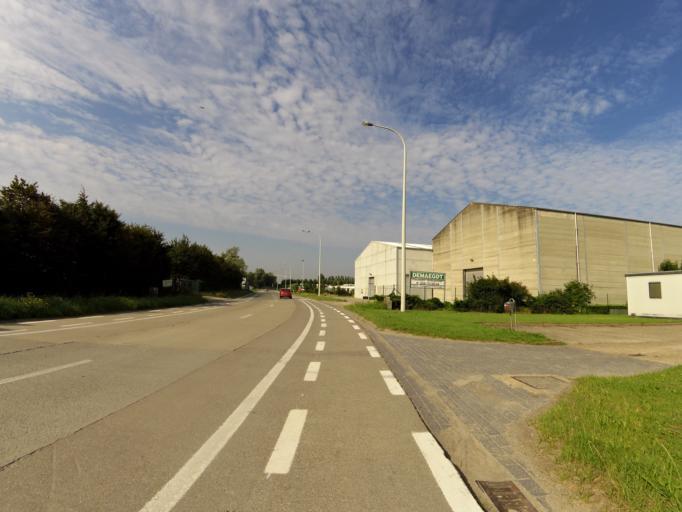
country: BE
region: Flanders
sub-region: Provincie West-Vlaanderen
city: Ostend
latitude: 51.2065
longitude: 2.9392
